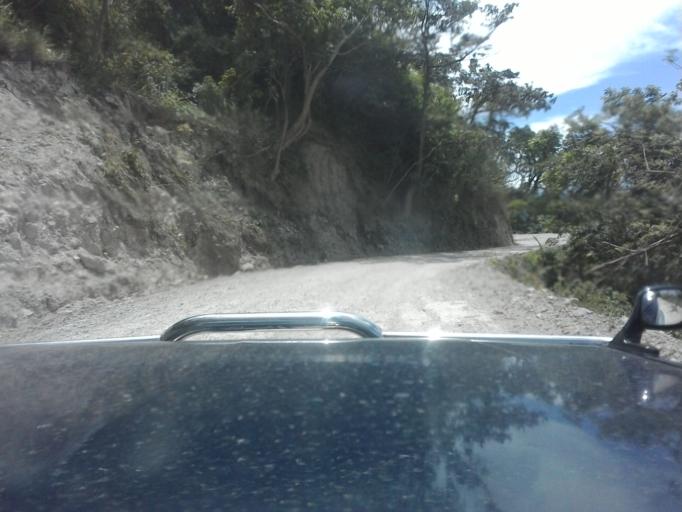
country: CR
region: Guanacaste
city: Juntas
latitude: 10.2501
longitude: -84.8391
